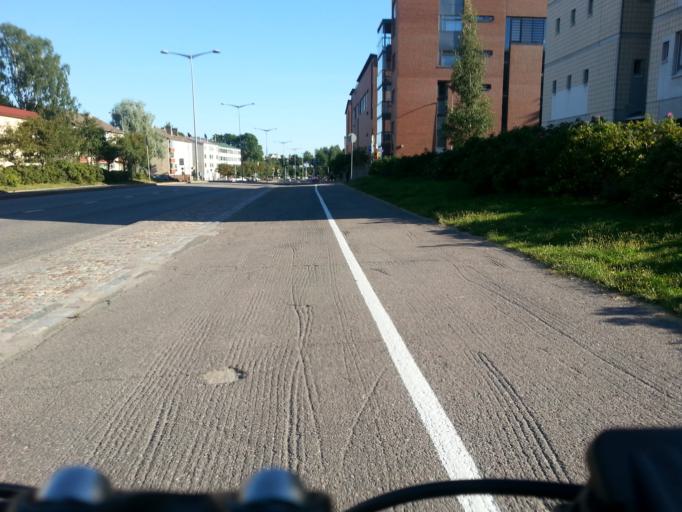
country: FI
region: Uusimaa
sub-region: Helsinki
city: Teekkarikylae
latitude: 60.2118
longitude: 24.8867
